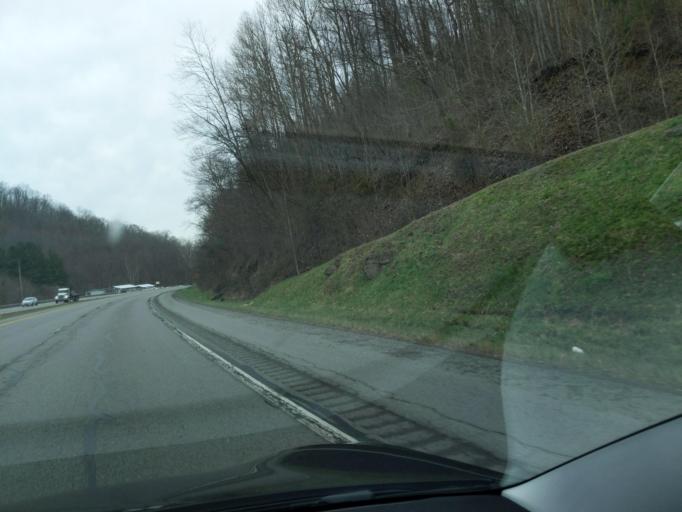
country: US
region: Kentucky
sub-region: Knox County
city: Barbourville
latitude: 36.8743
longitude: -83.8146
